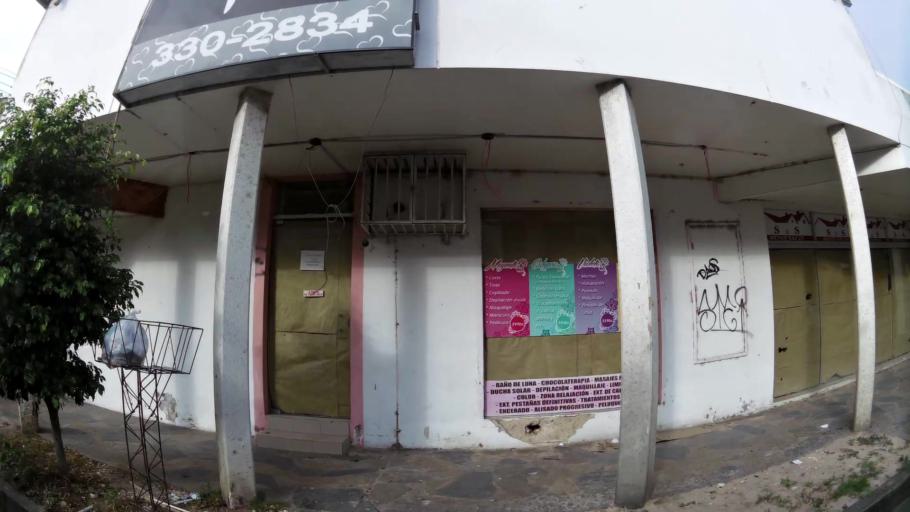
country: BO
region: Santa Cruz
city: Santa Cruz de la Sierra
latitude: -17.7850
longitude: -63.1732
